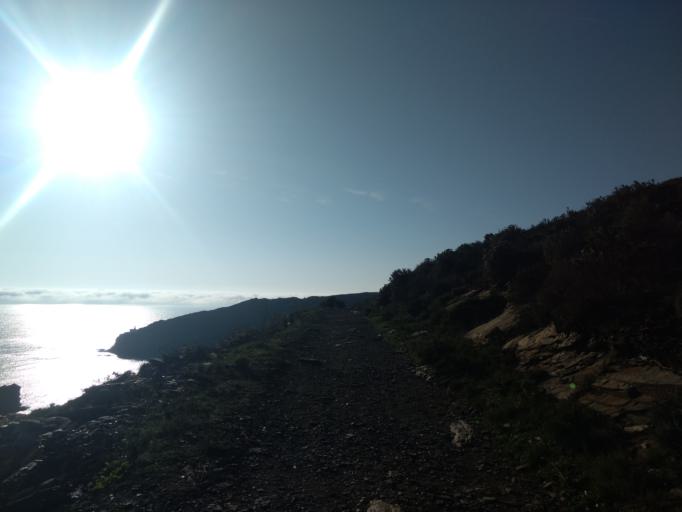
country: ES
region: Catalonia
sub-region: Provincia de Girona
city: Cadaques
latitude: 42.2757
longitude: 3.2788
